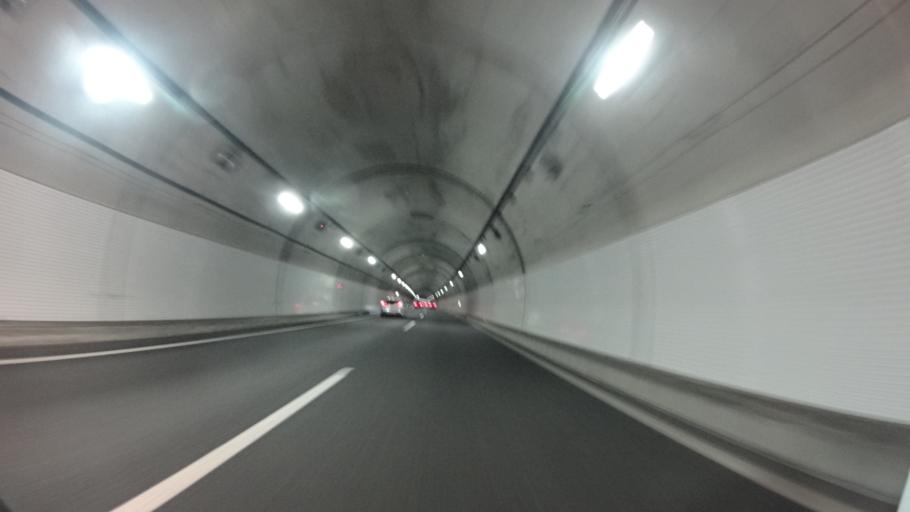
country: JP
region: Ehime
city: Saijo
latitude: 33.8932
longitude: 133.1980
